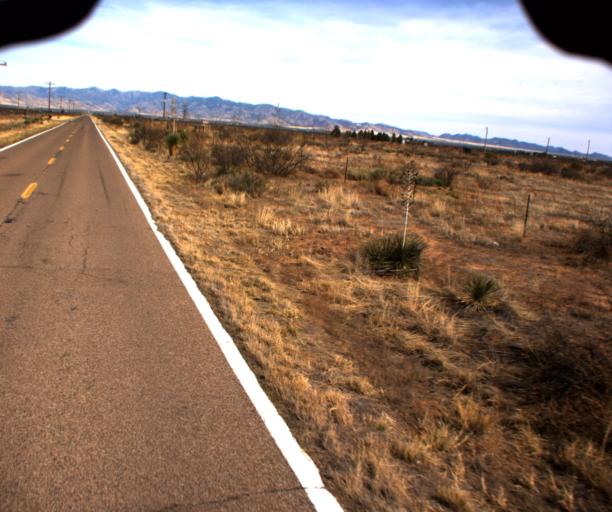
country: US
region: Arizona
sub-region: Cochise County
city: Willcox
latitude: 31.8762
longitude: -109.6123
